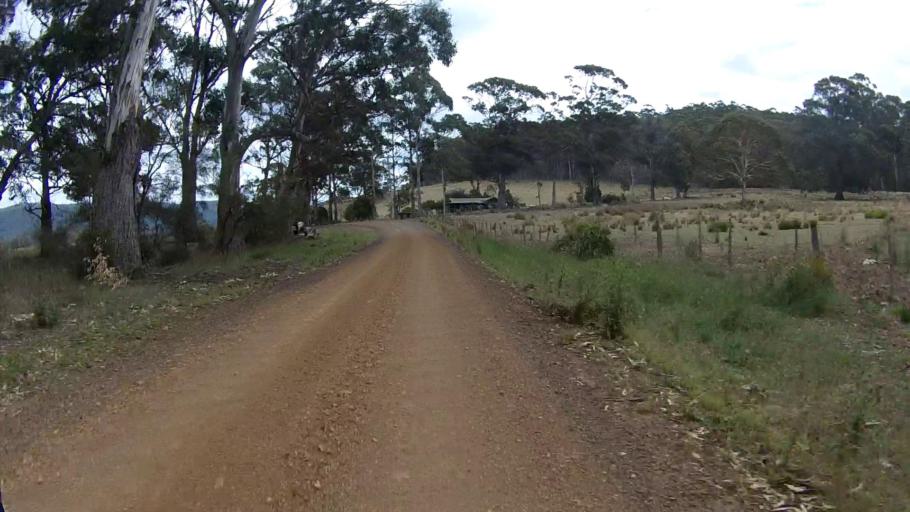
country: AU
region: Tasmania
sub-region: Sorell
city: Sorell
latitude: -42.6320
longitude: 147.9252
